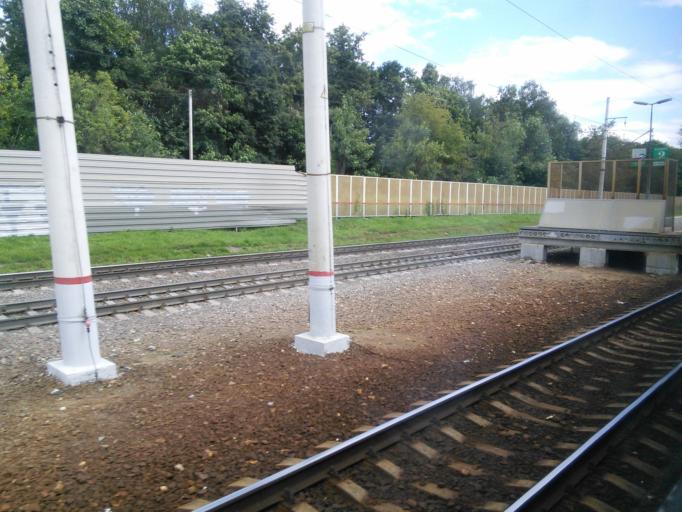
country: RU
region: Moscow
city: Zhulebino
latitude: 55.7000
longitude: 37.8614
